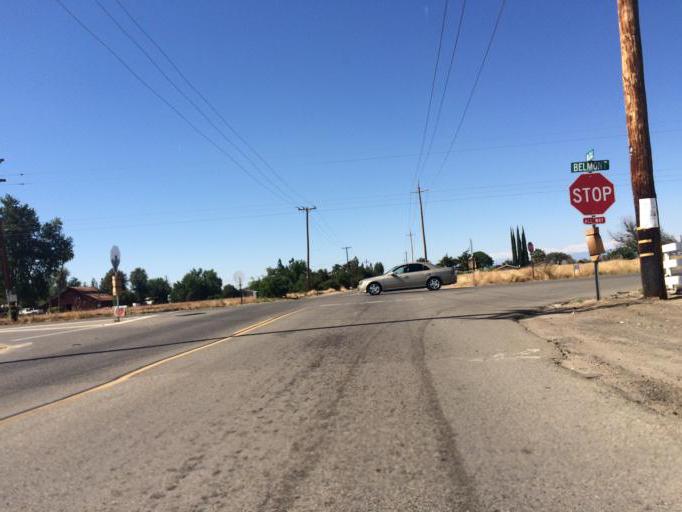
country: US
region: California
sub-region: Fresno County
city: Sanger
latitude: 36.7499
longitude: -119.6101
